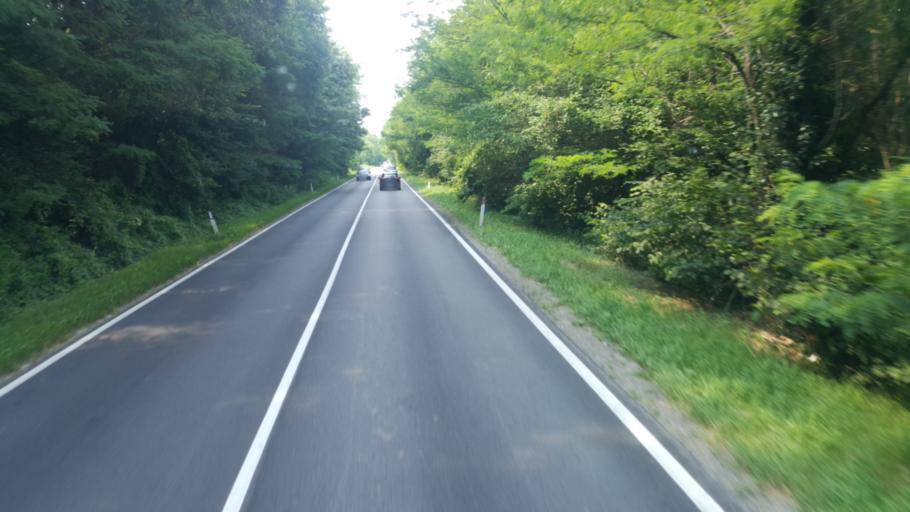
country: IT
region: Lombardy
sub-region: Provincia di Como
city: Oltrona di San Mamette
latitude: 45.7588
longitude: 8.9655
